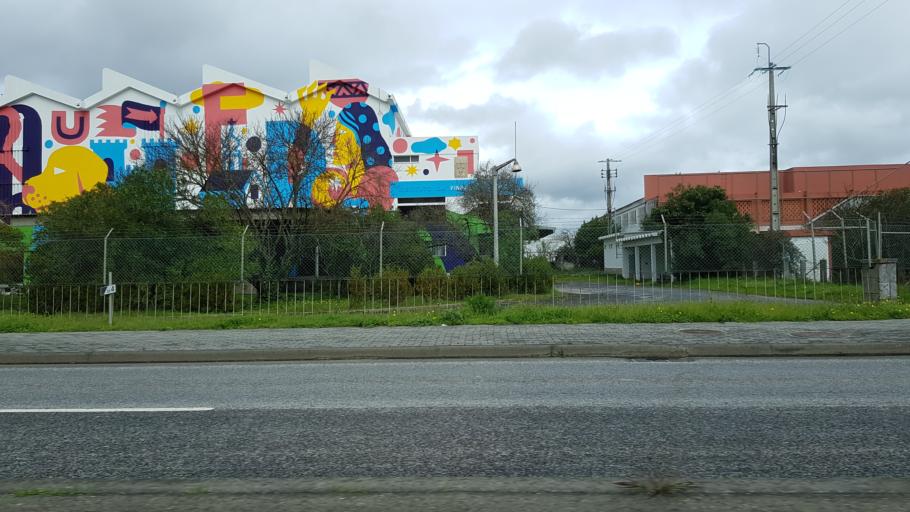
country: PT
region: Lisbon
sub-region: Alenquer
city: Carregado
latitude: 39.0381
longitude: -8.9847
